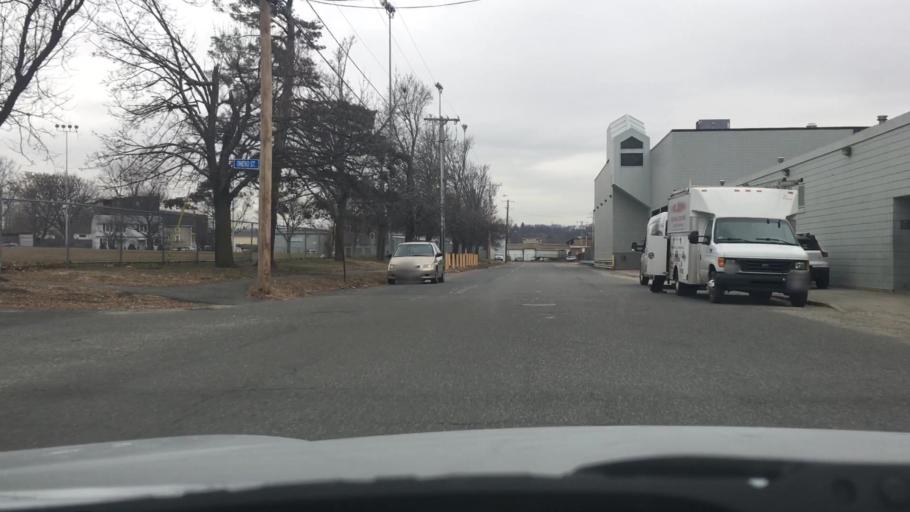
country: US
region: Massachusetts
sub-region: Hampden County
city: Holyoke
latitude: 42.2010
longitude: -72.5999
